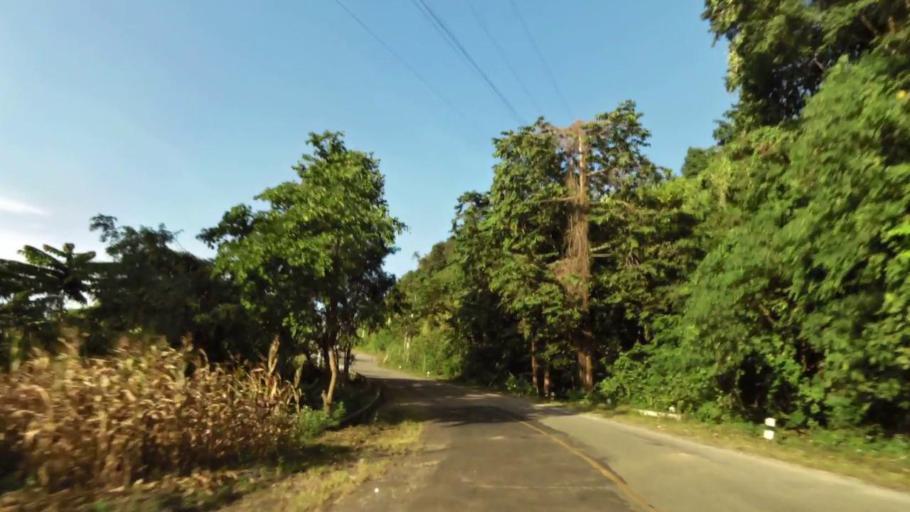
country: TH
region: Chiang Rai
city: Khun Tan
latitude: 19.8637
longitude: 100.4407
